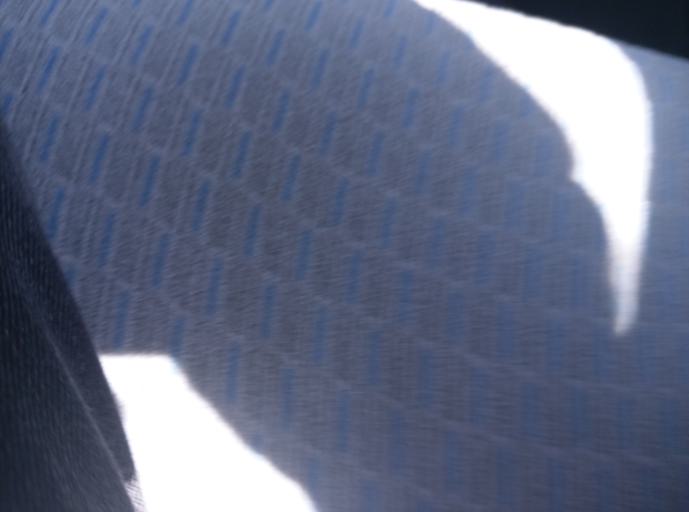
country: CD
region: Nord Kivu
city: Goma
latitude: -1.6474
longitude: 29.1692
